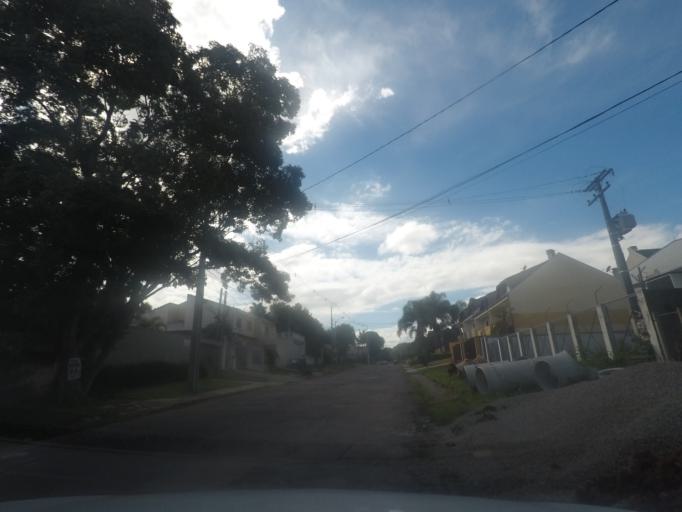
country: BR
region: Parana
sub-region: Pinhais
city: Pinhais
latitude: -25.4594
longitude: -49.2274
